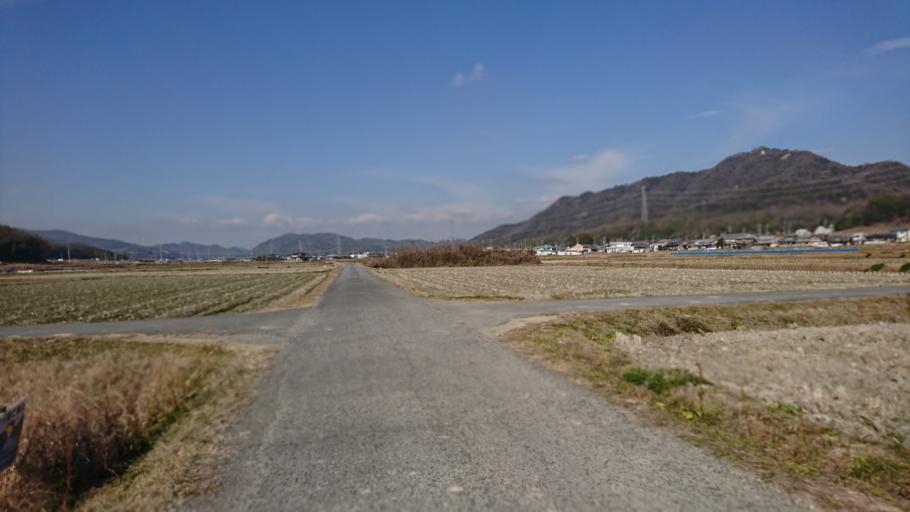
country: JP
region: Hyogo
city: Kakogawacho-honmachi
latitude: 34.8159
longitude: 134.8534
